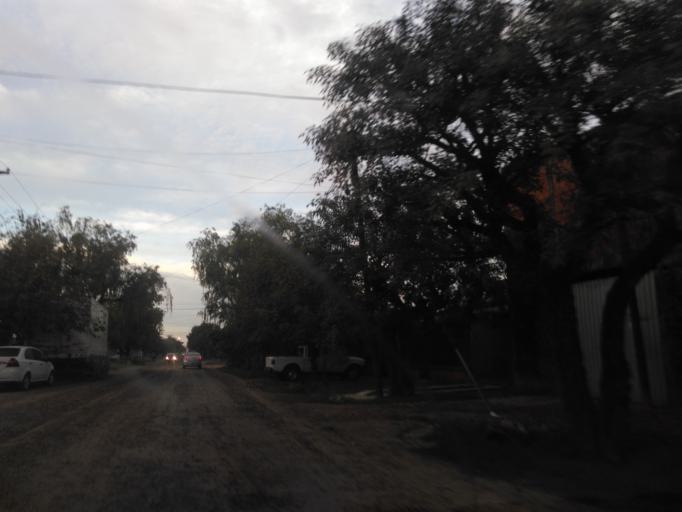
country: AR
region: Chaco
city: Resistencia
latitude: -27.4711
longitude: -58.9946
